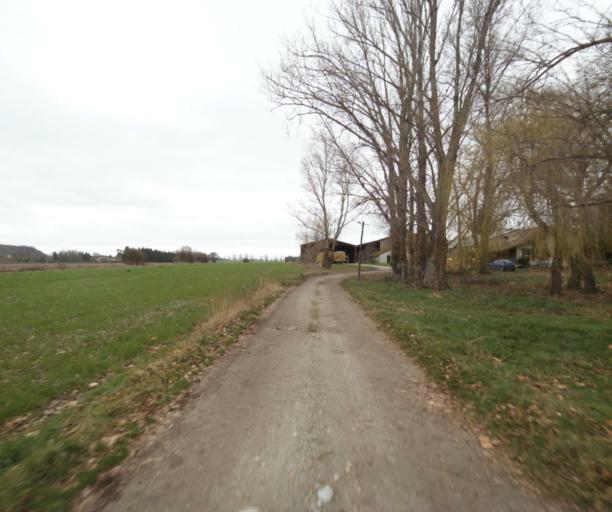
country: FR
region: Midi-Pyrenees
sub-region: Departement de l'Ariege
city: Saverdun
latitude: 43.1923
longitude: 1.6037
